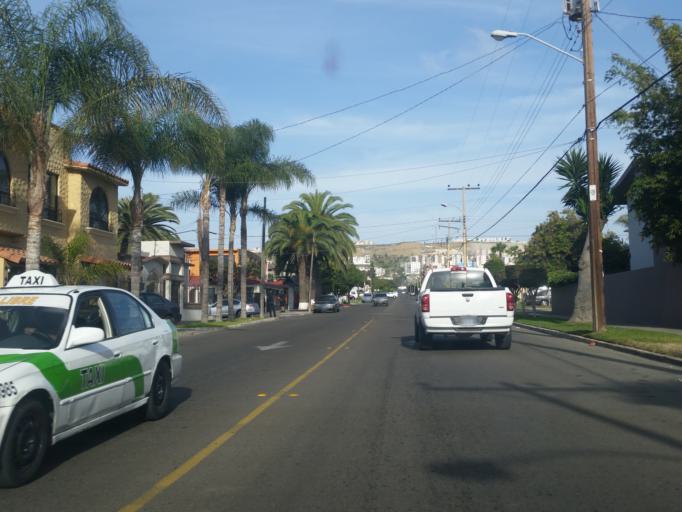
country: US
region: California
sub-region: San Diego County
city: Imperial Beach
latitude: 32.5250
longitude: -117.1183
